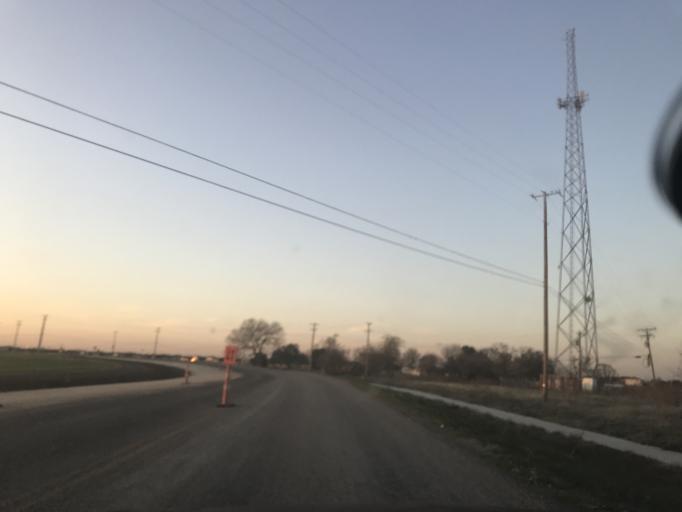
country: US
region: Texas
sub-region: Williamson County
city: Hutto
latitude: 30.5168
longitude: -97.5365
